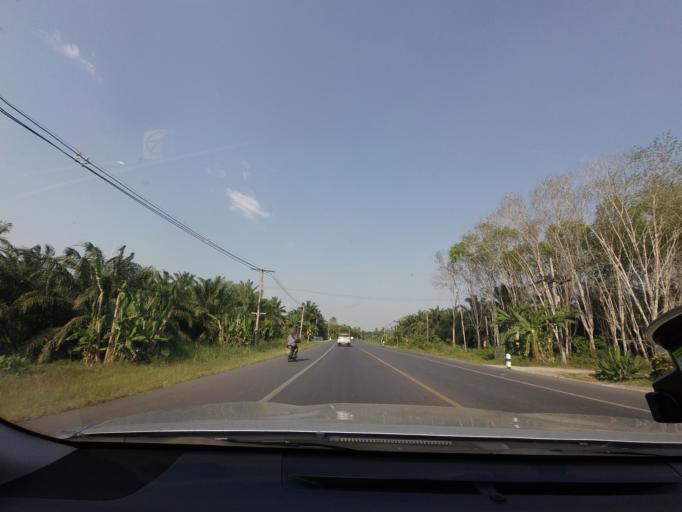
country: TH
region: Surat Thani
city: Phrasaeng
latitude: 8.5701
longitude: 99.1990
